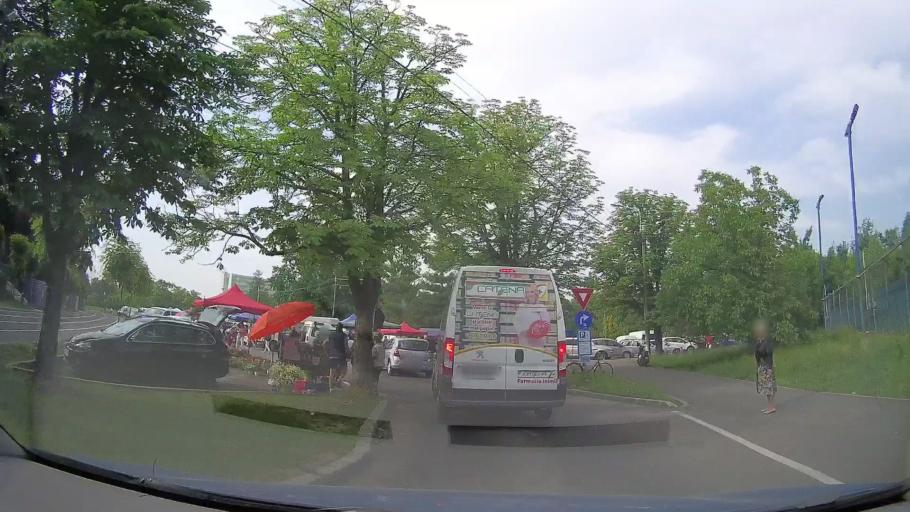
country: RO
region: Timis
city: Timisoara
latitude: 45.7408
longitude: 21.2424
